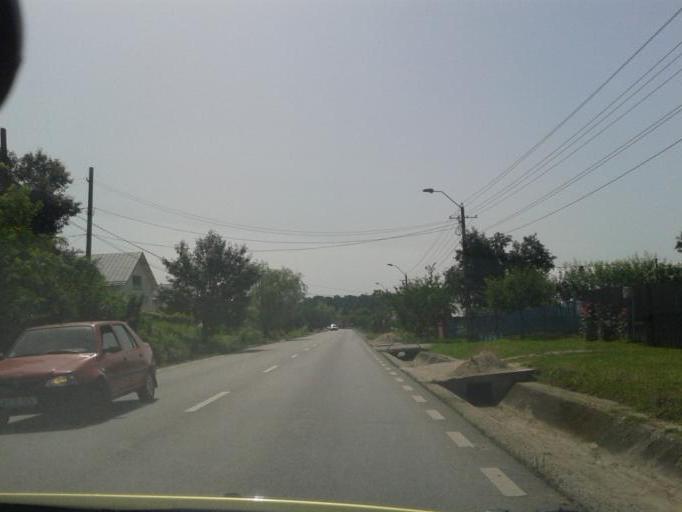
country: RO
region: Arges
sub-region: Comuna Babana
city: Babana
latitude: 44.8965
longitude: 24.7400
